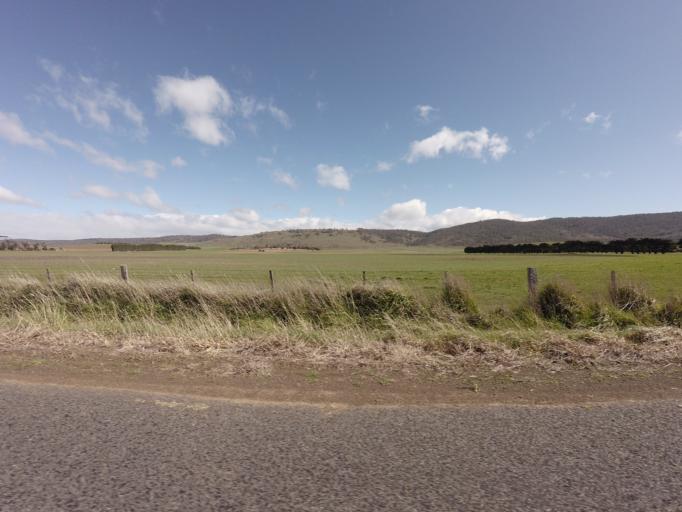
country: AU
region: Tasmania
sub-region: Northern Midlands
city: Evandale
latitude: -41.9958
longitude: 147.4545
